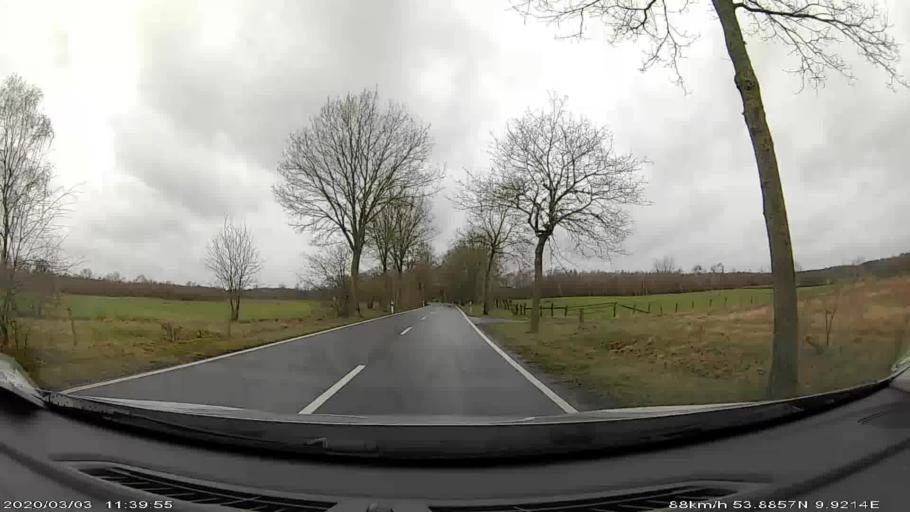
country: DE
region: Schleswig-Holstein
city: Nutzen
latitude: 53.8868
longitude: 9.9166
